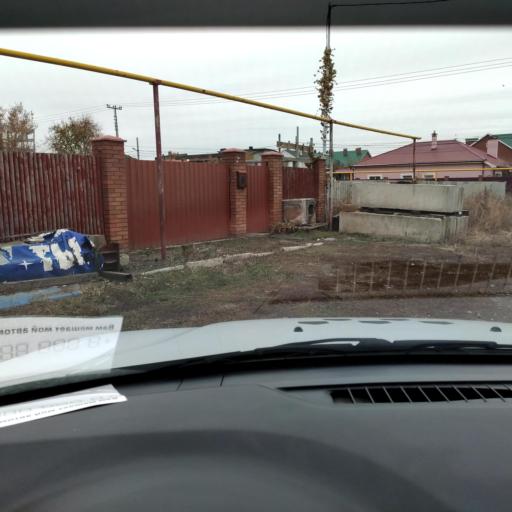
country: RU
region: Samara
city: Podstepki
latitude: 53.5131
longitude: 49.2084
